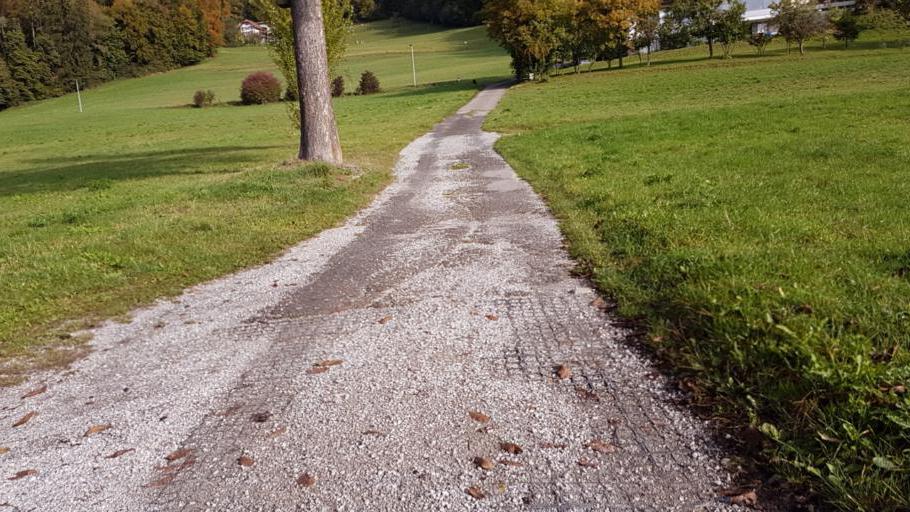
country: CH
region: Bern
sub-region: Bern-Mittelland District
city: Stettlen
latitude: 46.9327
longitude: 7.5313
